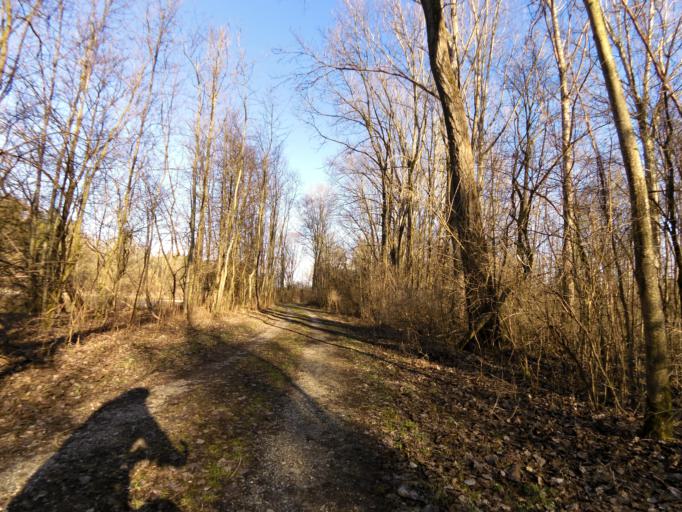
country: DE
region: Bavaria
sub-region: Lower Bavaria
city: Tiefenbach
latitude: 48.5172
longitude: 12.0920
